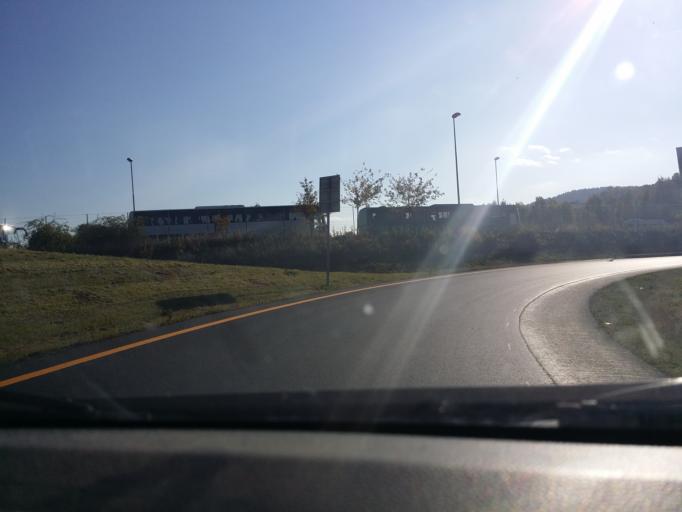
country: NO
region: Akershus
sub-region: Baerum
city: Skui
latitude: 59.9231
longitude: 10.4616
